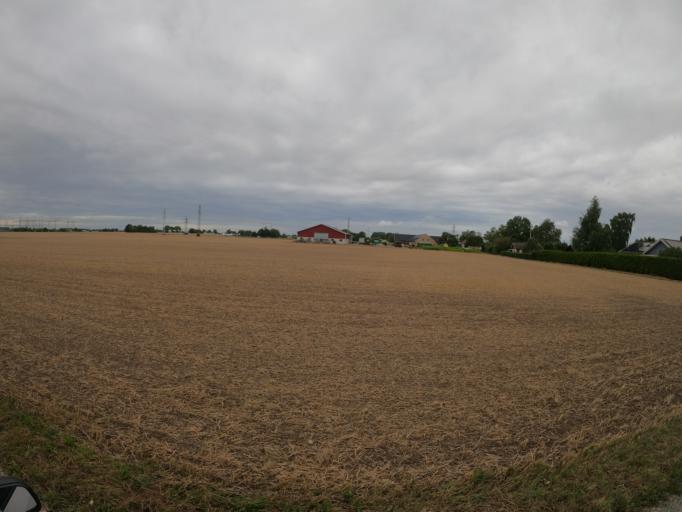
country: SE
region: Skane
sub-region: Lunds Kommun
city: Lund
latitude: 55.7449
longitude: 13.1487
